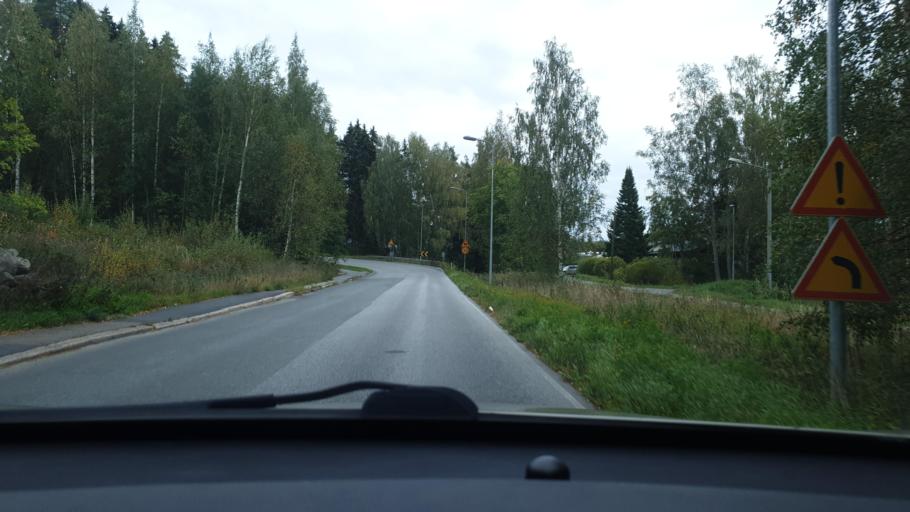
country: FI
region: Ostrobothnia
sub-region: Vaasa
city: Korsholm
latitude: 63.0973
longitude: 21.6617
